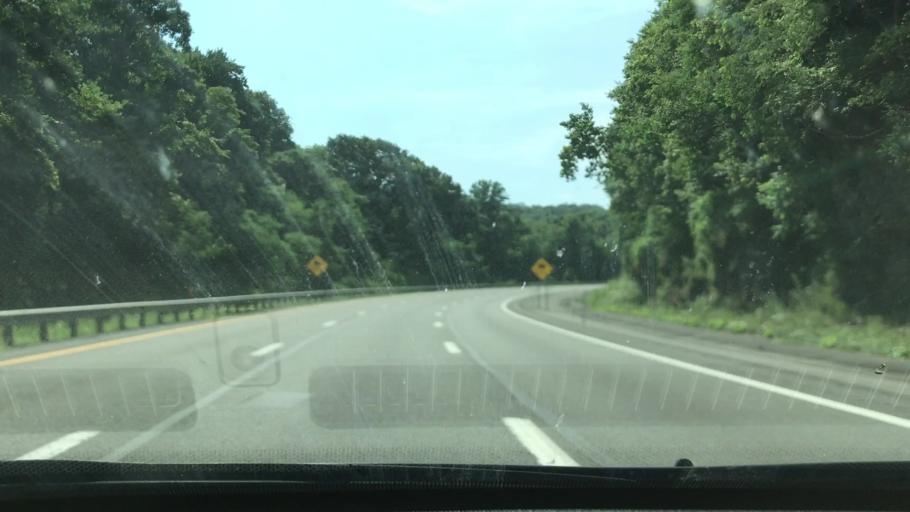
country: US
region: West Virginia
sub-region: Raleigh County
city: Shady Spring
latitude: 37.6956
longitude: -81.1330
